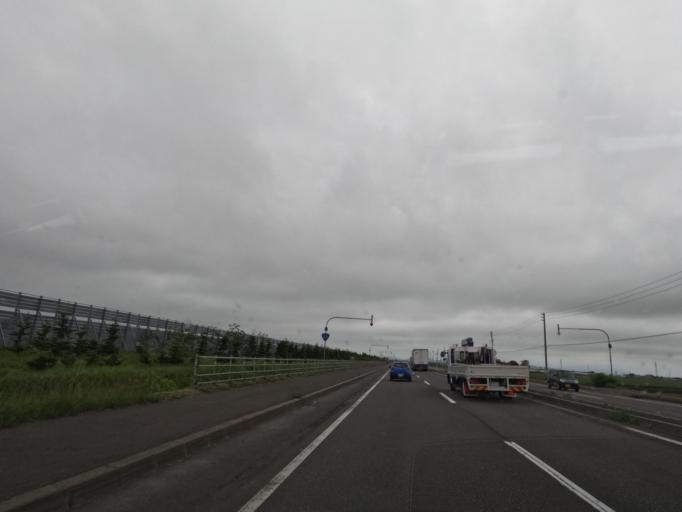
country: JP
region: Hokkaido
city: Tobetsu
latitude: 43.1698
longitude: 141.5201
